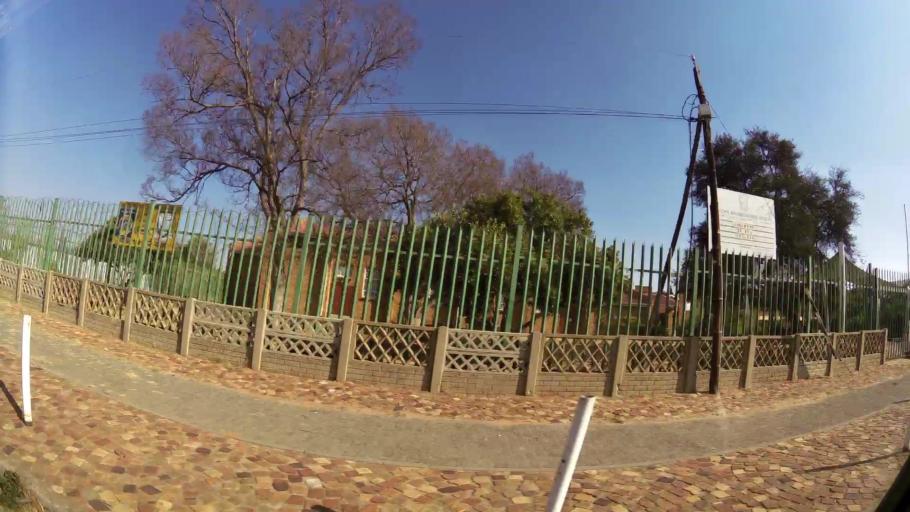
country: ZA
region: Gauteng
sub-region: City of Johannesburg Metropolitan Municipality
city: Johannesburg
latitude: -26.2617
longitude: 28.0215
